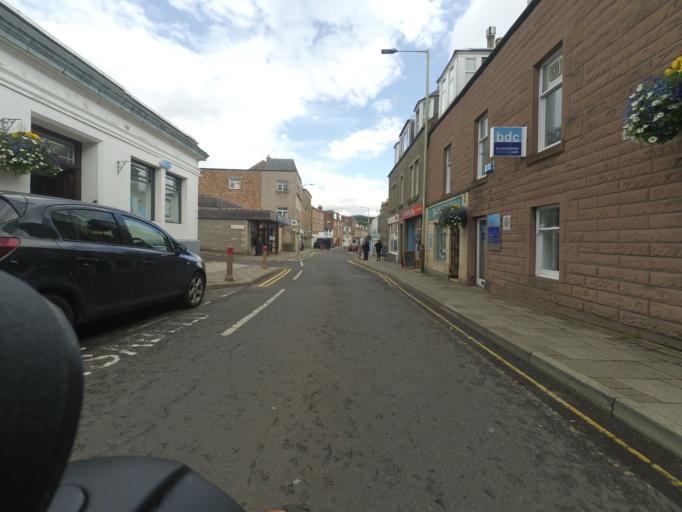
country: GB
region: Scotland
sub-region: Perth and Kinross
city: Blairgowrie
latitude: 56.5918
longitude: -3.3402
